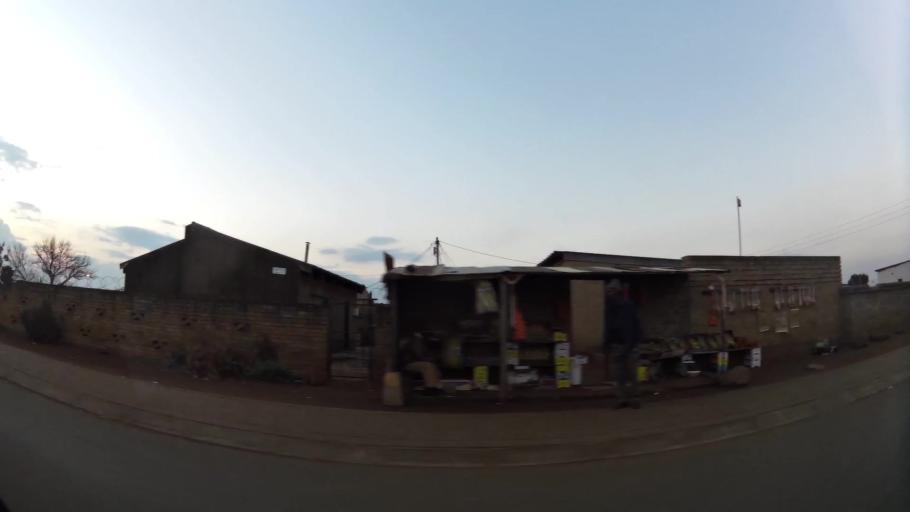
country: ZA
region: Gauteng
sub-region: City of Johannesburg Metropolitan Municipality
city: Orange Farm
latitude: -26.5541
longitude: 27.8515
